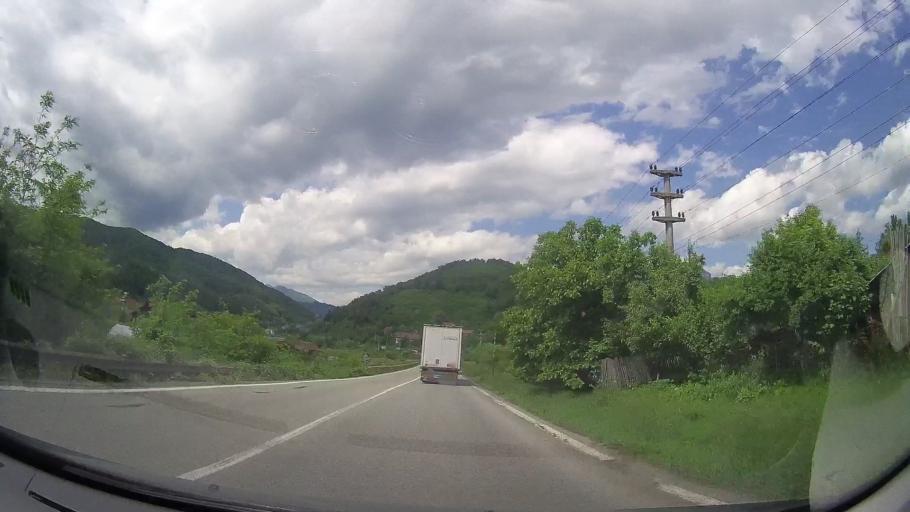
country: RO
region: Valcea
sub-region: Oras Calimanesti
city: Jiblea Veche
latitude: 45.2443
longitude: 24.3485
